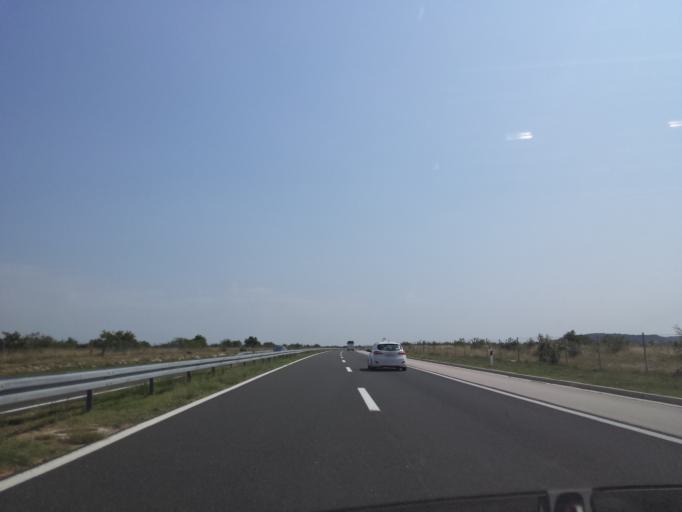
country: HR
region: Zadarska
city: Polaca
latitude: 44.0921
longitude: 15.4880
